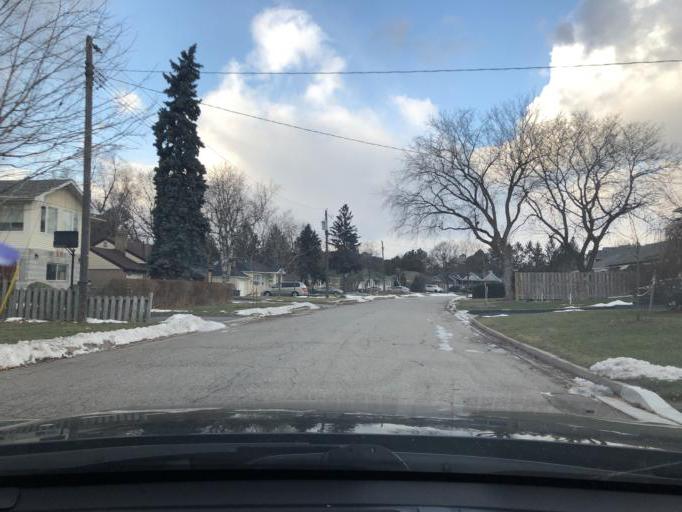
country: CA
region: Ontario
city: Scarborough
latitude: 43.7771
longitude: -79.2900
